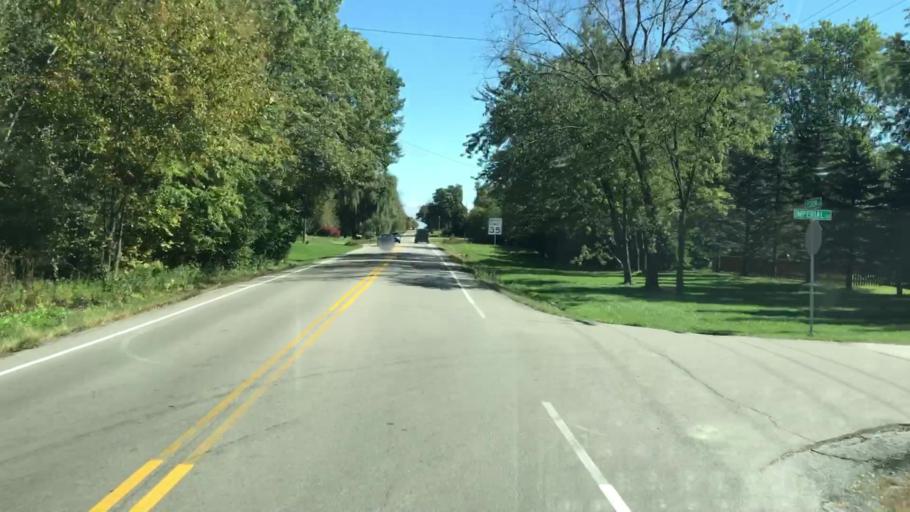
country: US
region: Wisconsin
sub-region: Waukesha County
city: Brookfield
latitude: 43.1046
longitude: -88.1344
